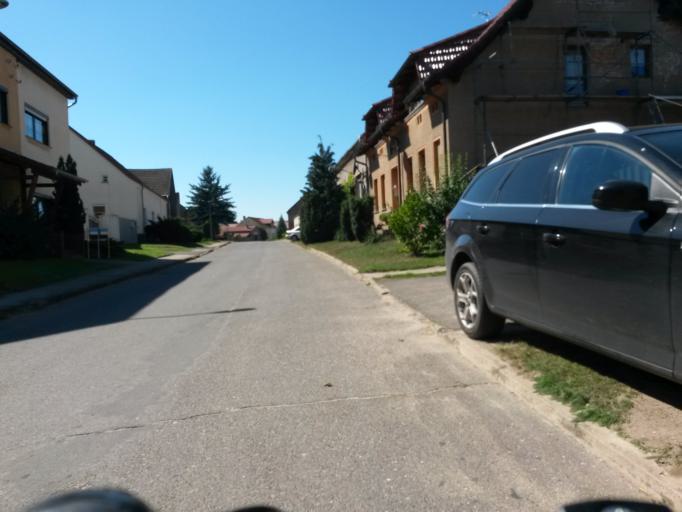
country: DE
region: Brandenburg
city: Schoneberg
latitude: 52.9232
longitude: 14.1246
